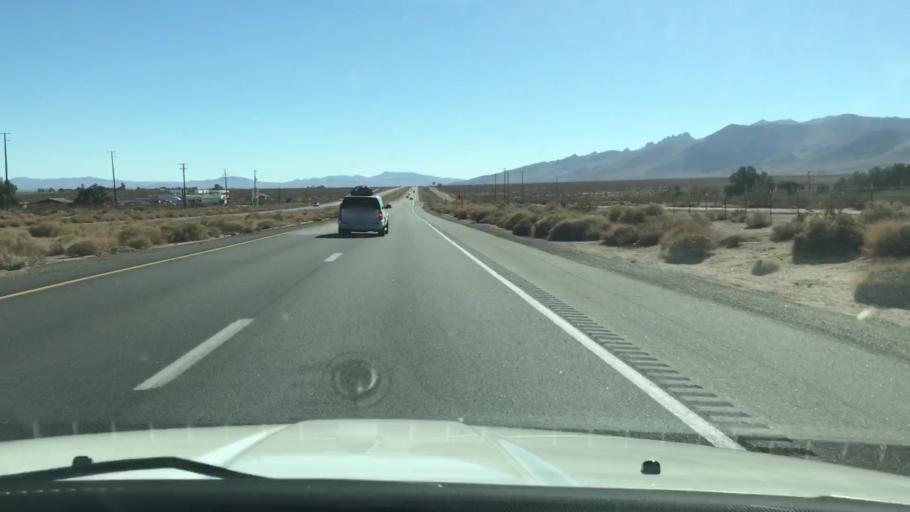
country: US
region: California
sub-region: Kern County
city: Inyokern
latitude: 35.8021
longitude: -117.8732
